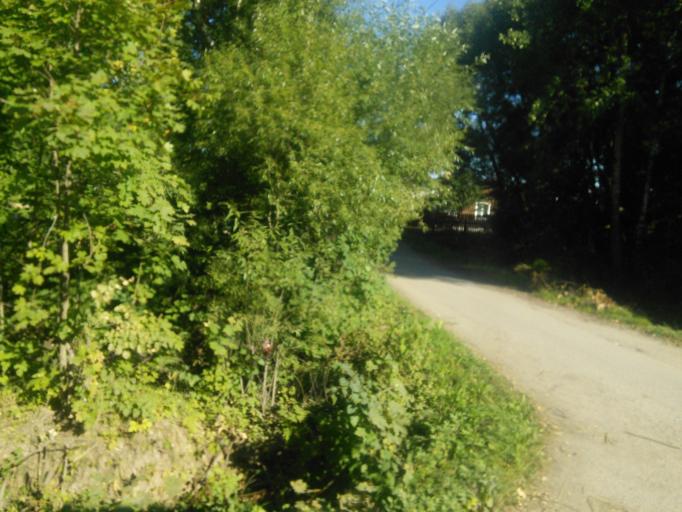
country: RU
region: Tverskaya
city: Kesova Gora
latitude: 57.5914
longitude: 37.2914
